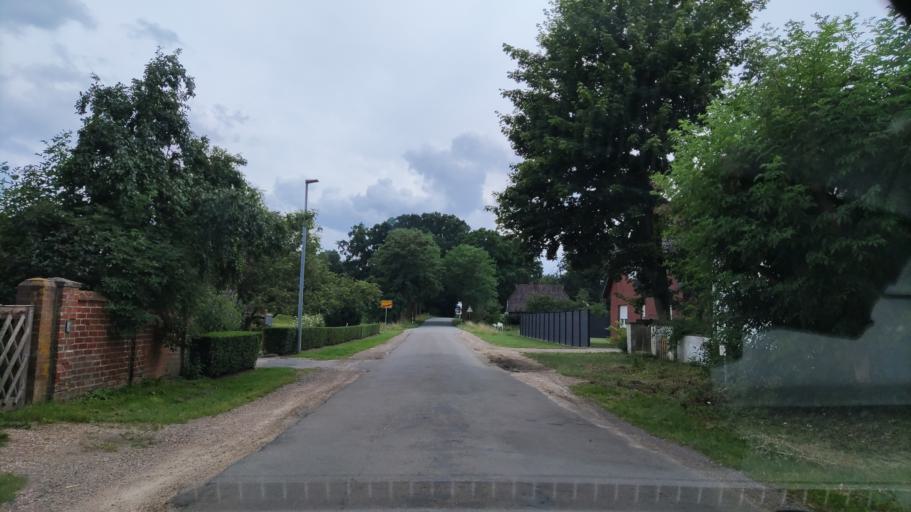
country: DE
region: Lower Saxony
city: Dannenberg
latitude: 53.0970
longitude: 11.1259
